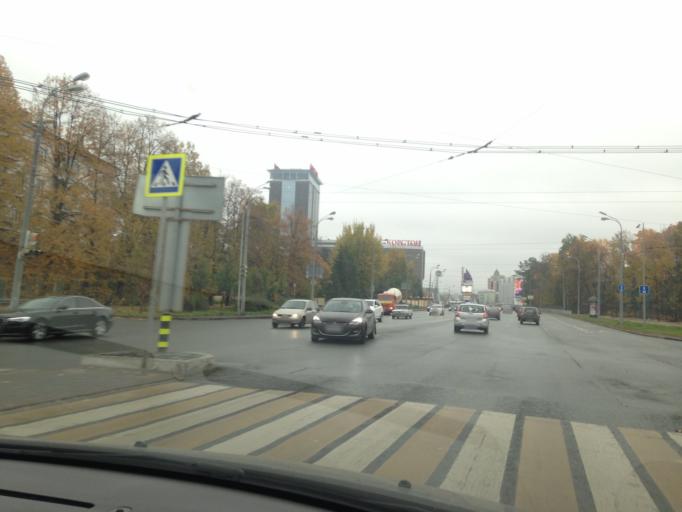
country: RU
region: Tatarstan
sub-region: Gorod Kazan'
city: Kazan
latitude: 55.7944
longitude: 49.1430
